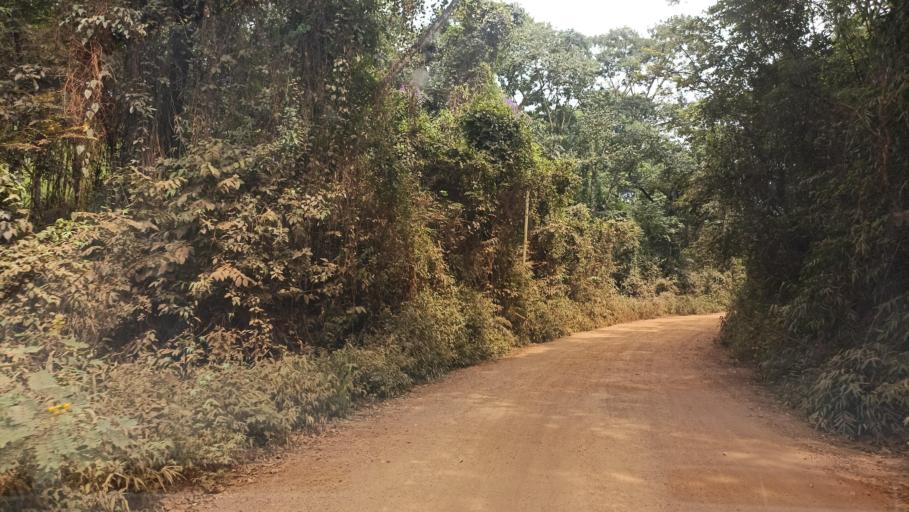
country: BR
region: Minas Gerais
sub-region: Itabirito
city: Itabirito
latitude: -20.3723
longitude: -43.7615
